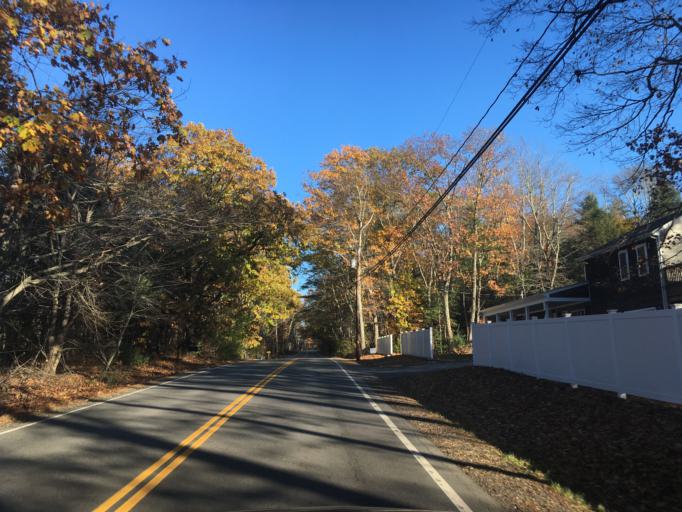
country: US
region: New Hampshire
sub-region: Rockingham County
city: Stratham Station
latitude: 43.0387
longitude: -70.9119
